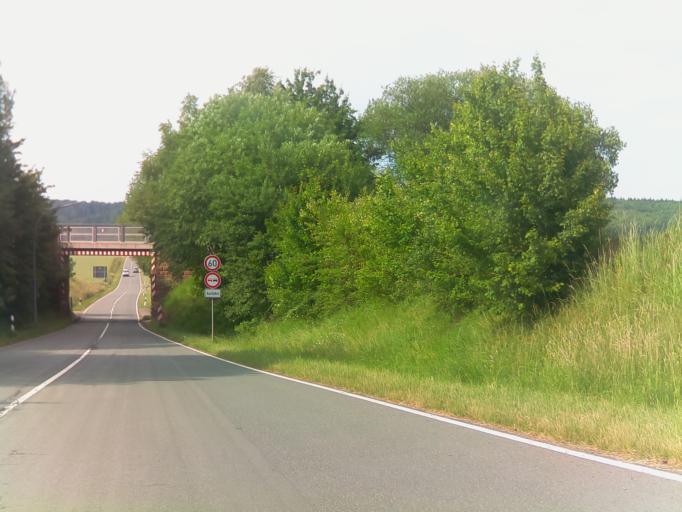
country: DE
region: Hesse
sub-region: Regierungsbezirk Kassel
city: Waldeck
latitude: 51.2297
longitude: 9.0878
